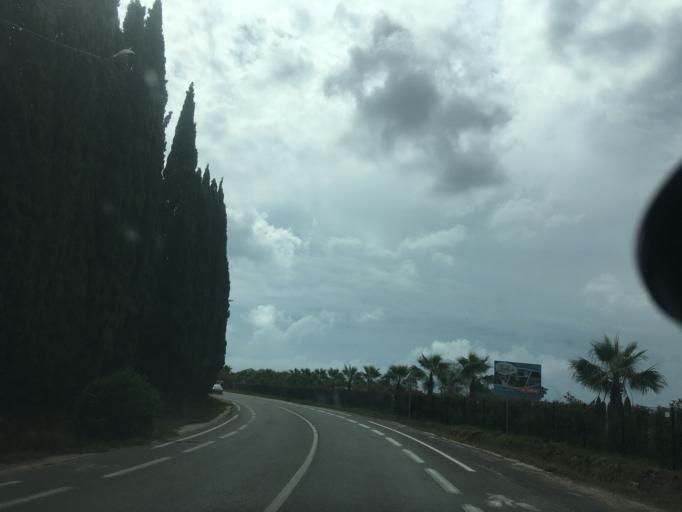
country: FR
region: Provence-Alpes-Cote d'Azur
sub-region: Departement du Var
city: La Londe-les-Maures
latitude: 43.1292
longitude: 6.2405
